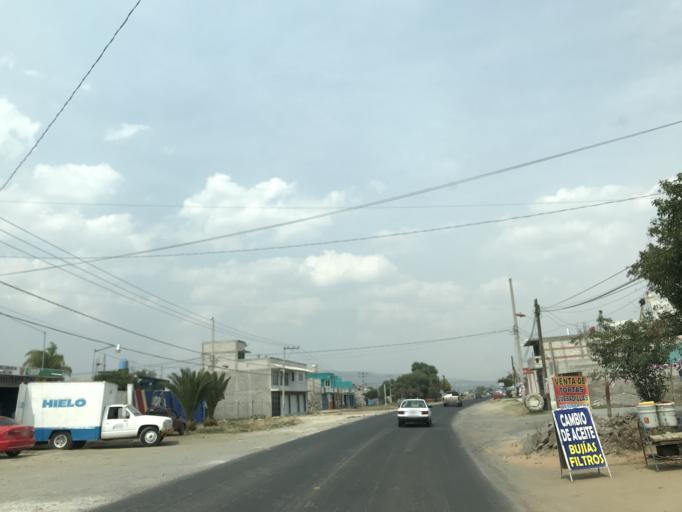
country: MX
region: Tlaxcala
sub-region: Ixtacuixtla de Mariano Matamoros
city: Santa Justina Ecatepec
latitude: 19.3103
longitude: -98.3503
